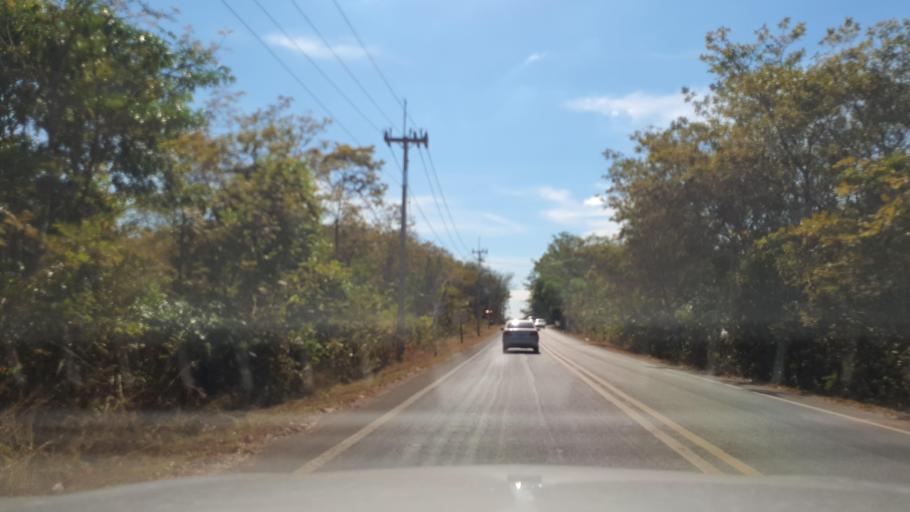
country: TH
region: Kalasin
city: Khao Wong
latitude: 16.7627
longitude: 104.1312
